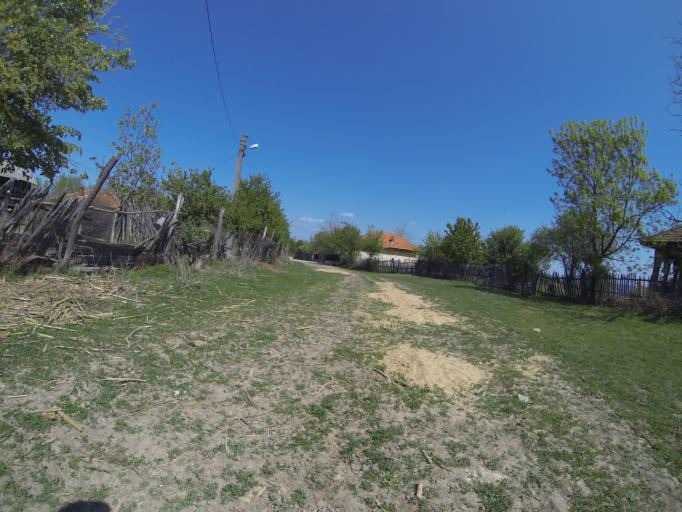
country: RO
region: Gorj
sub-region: Comuna Crusetu
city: Crusetu
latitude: 44.5876
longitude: 23.6609
